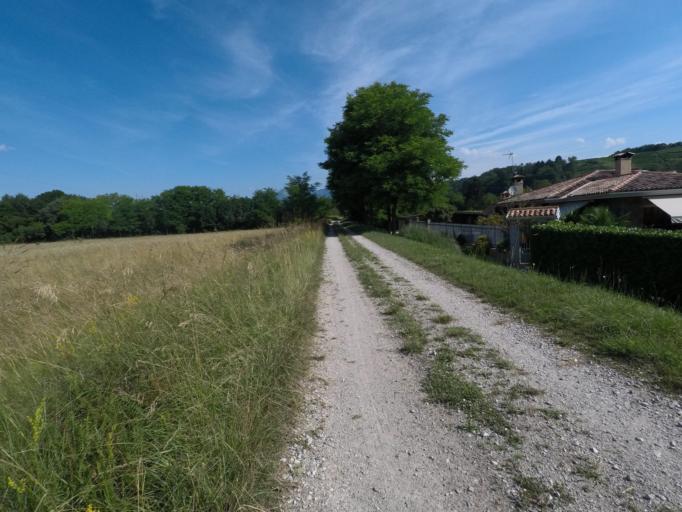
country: IT
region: Friuli Venezia Giulia
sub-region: Provincia di Udine
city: Reana del Rojale
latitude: 46.1647
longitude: 13.2623
